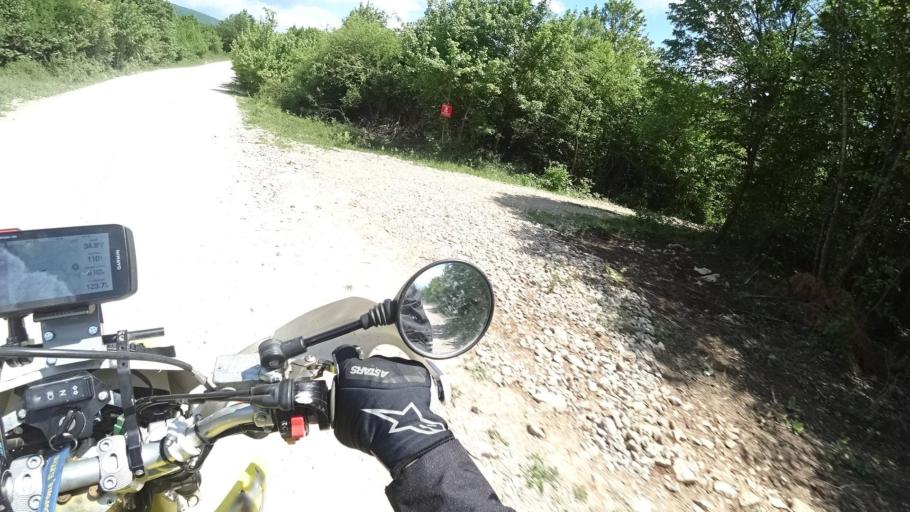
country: BA
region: Federation of Bosnia and Herzegovina
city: Bihac
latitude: 44.8321
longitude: 15.9280
